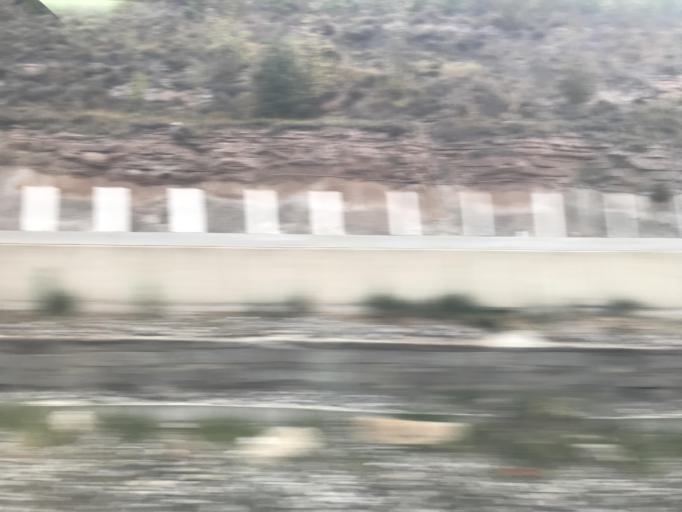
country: ES
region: Castille and Leon
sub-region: Provincia de Burgos
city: Briviesca
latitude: 42.5479
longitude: -3.3189
